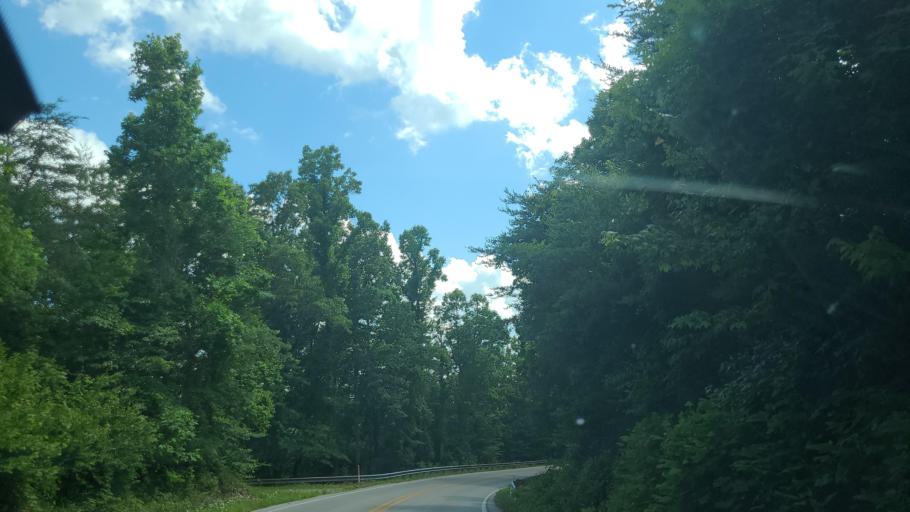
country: US
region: Kentucky
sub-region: Whitley County
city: Williamsburg
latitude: 36.8414
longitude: -84.2974
